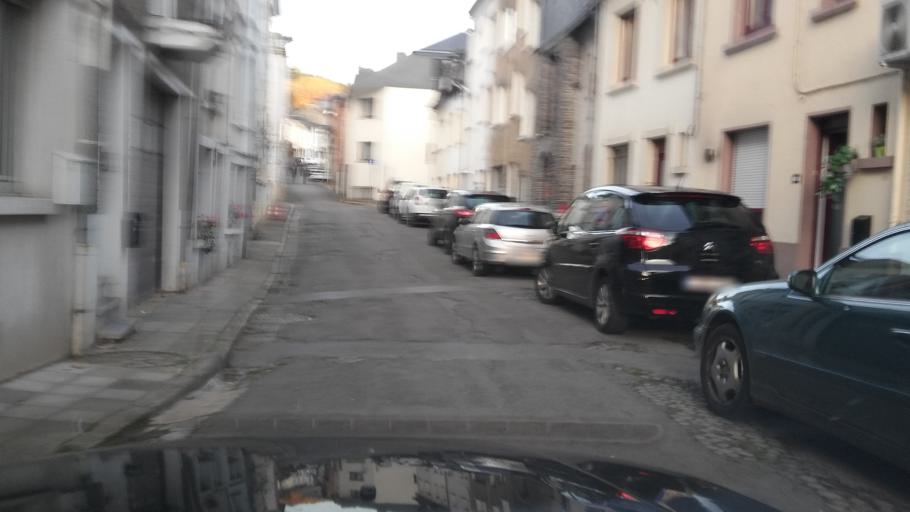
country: BE
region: Wallonia
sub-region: Province du Luxembourg
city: Bouillon
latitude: 49.7927
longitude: 5.0663
